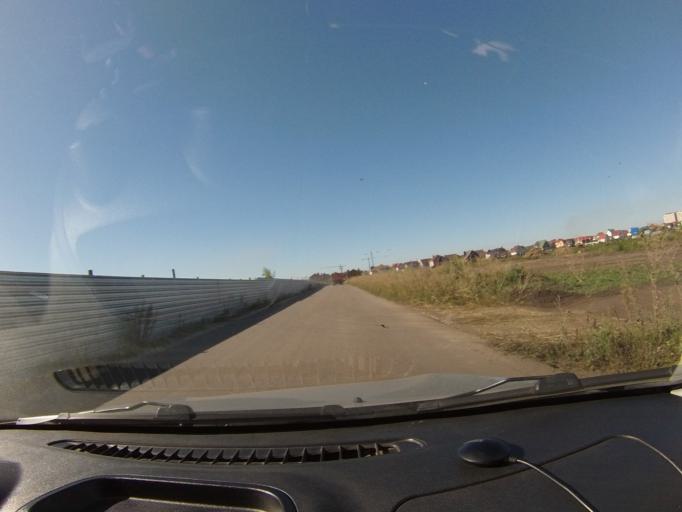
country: RU
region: Tambov
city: Tambov
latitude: 52.7638
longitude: 41.3879
